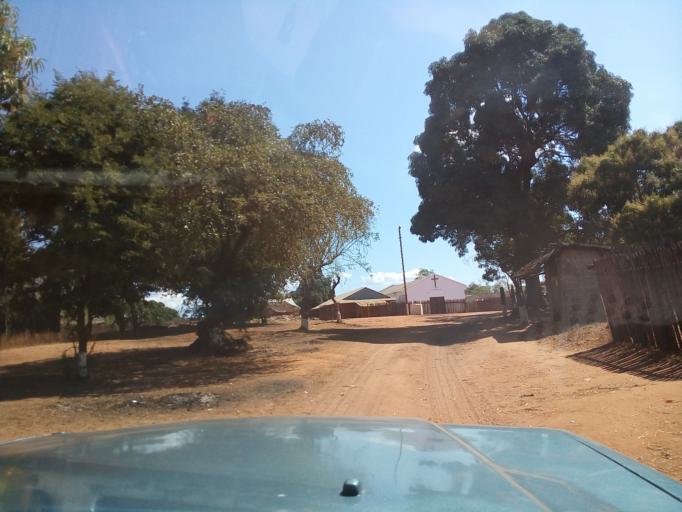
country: MG
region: Boeny
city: Mahajanga
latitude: -15.9595
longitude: 45.9399
